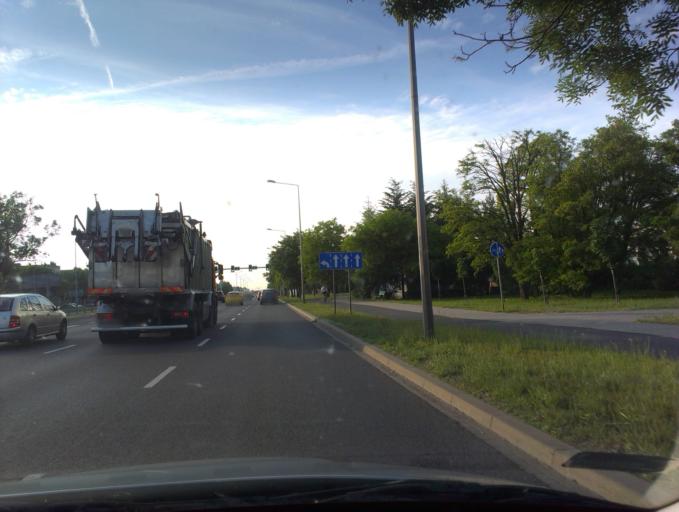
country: PL
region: Greater Poland Voivodeship
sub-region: Leszno
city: Leszno
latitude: 51.8372
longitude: 16.5955
